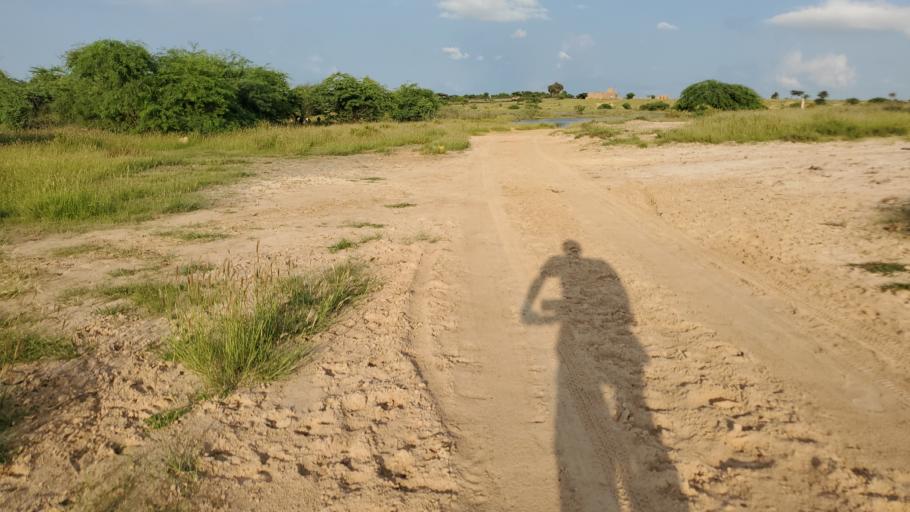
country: SN
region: Saint-Louis
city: Saint-Louis
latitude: 16.0495
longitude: -16.4187
